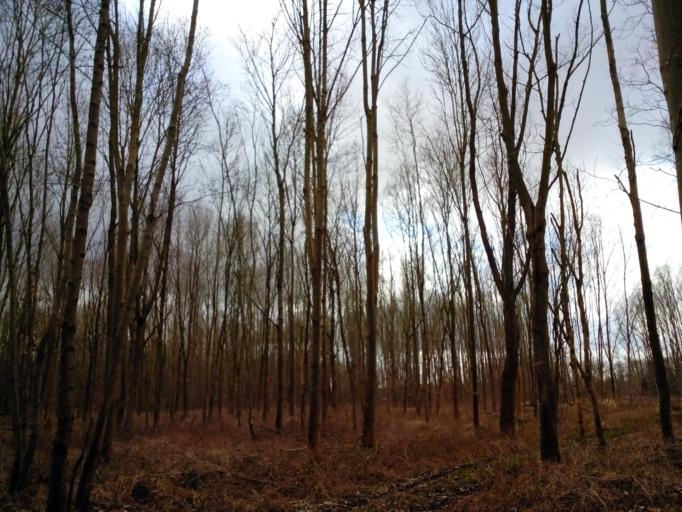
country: BE
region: Flanders
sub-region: Provincie Vlaams-Brabant
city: Oud-Heverlee
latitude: 50.8638
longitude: 4.6709
